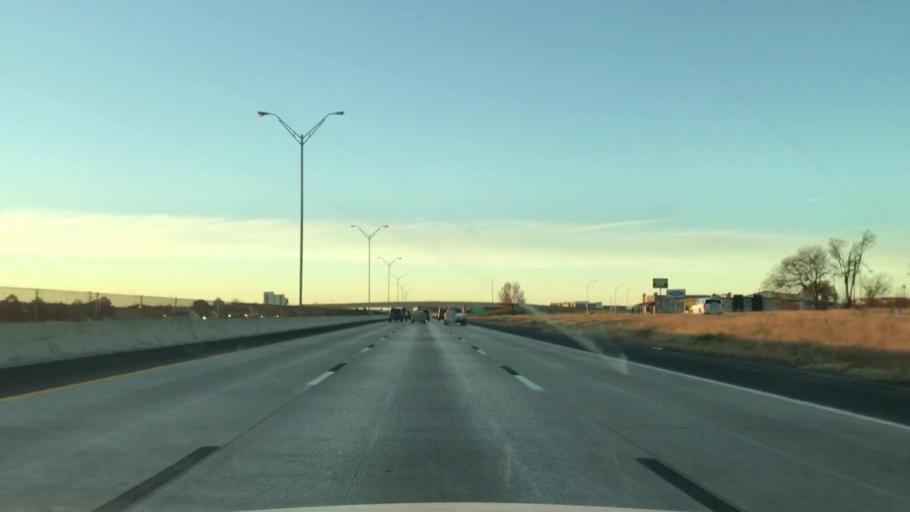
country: US
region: Texas
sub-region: Johnson County
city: Burleson
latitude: 32.5824
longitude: -97.3197
